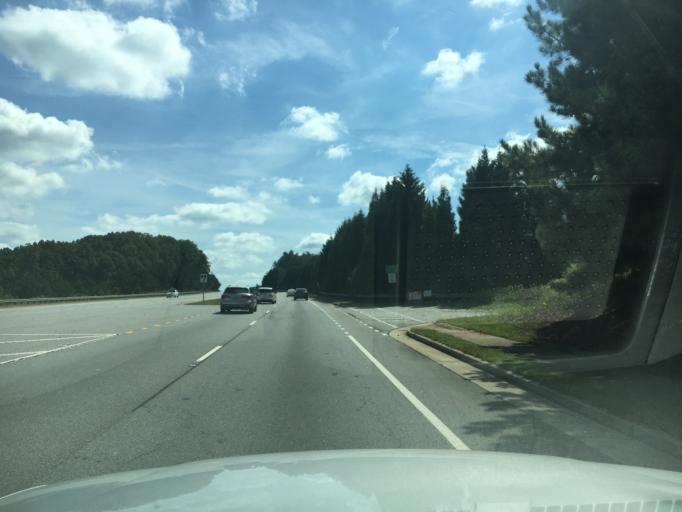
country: US
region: Georgia
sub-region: Gwinnett County
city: Duluth
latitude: 34.0180
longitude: -84.1157
